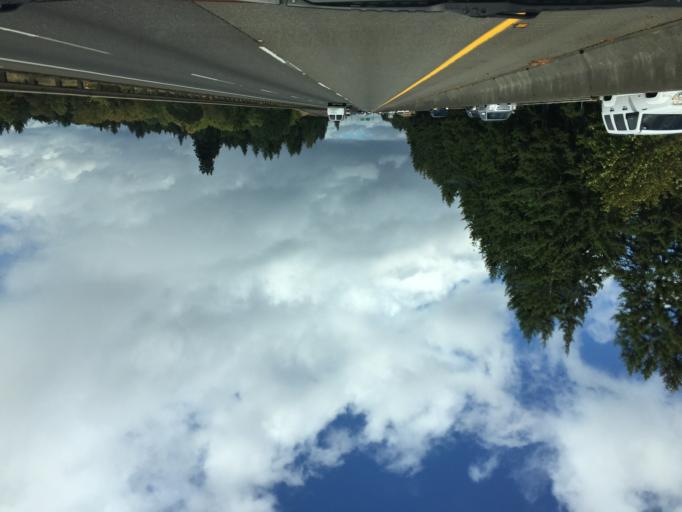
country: US
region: Washington
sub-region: Lewis County
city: Winlock
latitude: 46.4268
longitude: -122.8903
